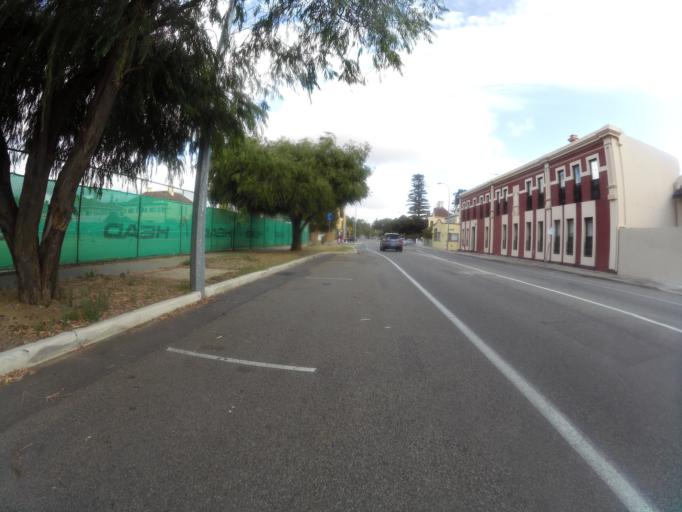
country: AU
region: Western Australia
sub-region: Fremantle
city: Fremantle
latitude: -32.0515
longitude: 115.7509
